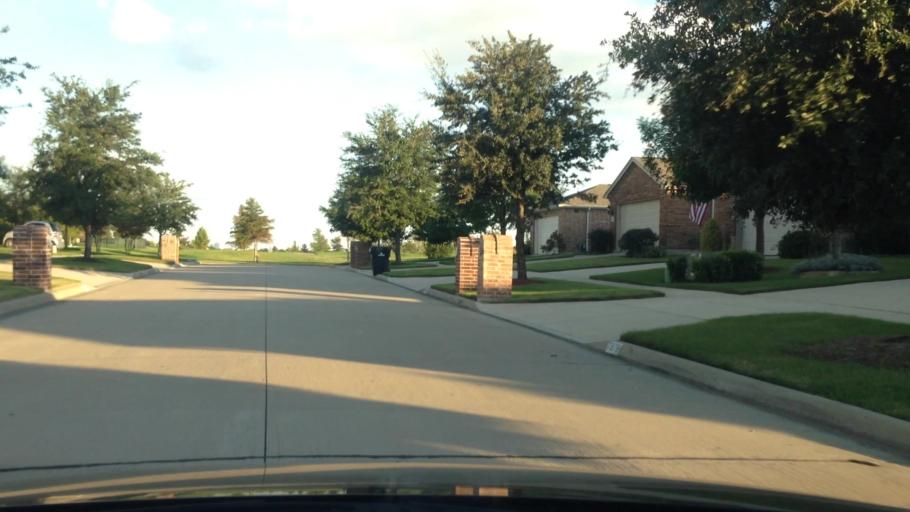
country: US
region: Texas
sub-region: Denton County
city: Little Elm
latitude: 33.1451
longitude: -96.9030
